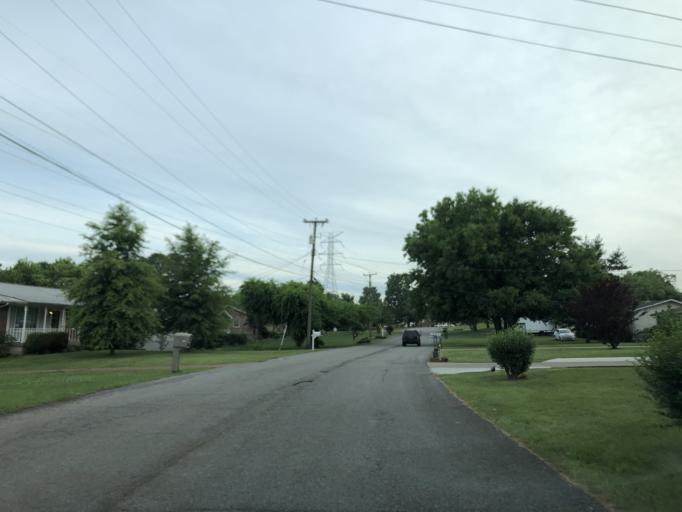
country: US
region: Tennessee
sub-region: Davidson County
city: Goodlettsville
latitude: 36.2963
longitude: -86.7132
